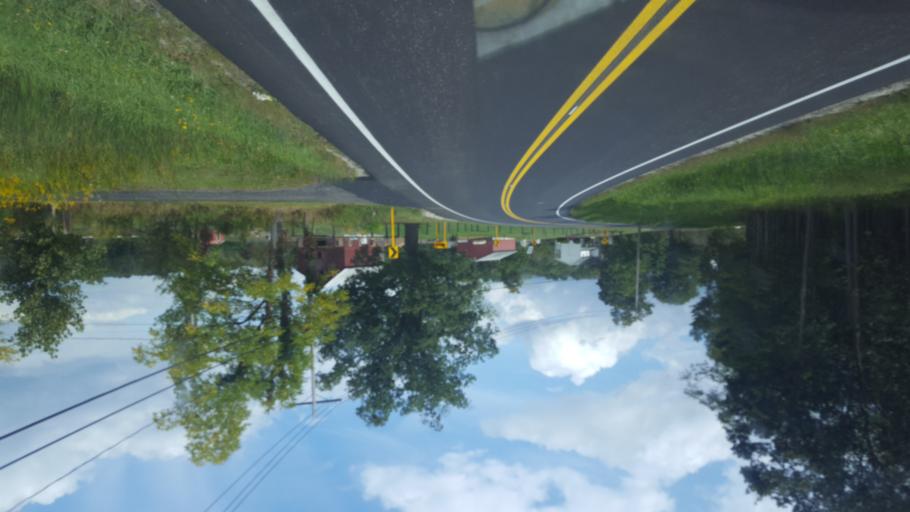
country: US
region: Ohio
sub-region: Geauga County
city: Burton
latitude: 41.4557
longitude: -81.1303
